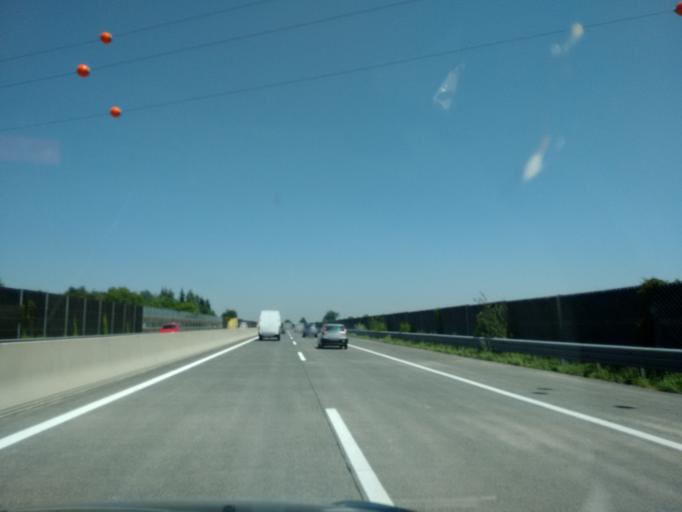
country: AT
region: Upper Austria
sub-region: Politischer Bezirk Gmunden
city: Vorchdorf
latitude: 48.0205
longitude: 13.9552
